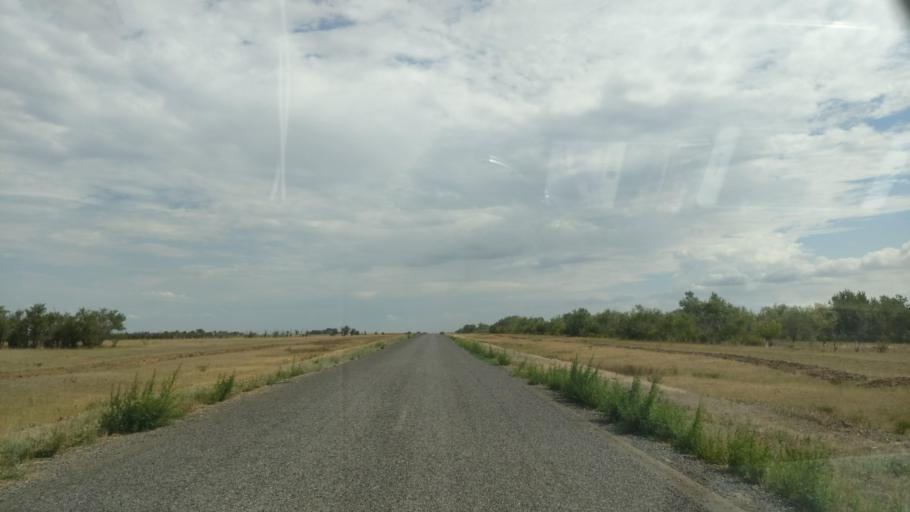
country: KZ
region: Pavlodar
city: Pavlodar
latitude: 52.6383
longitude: 77.0012
